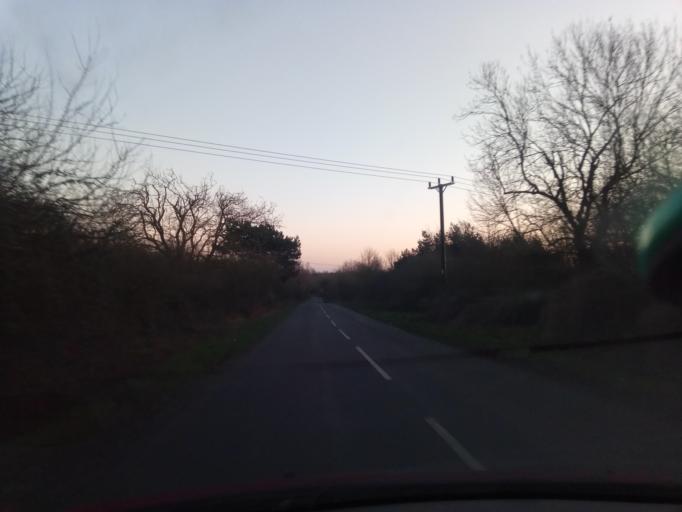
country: GB
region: England
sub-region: Leicestershire
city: Sileby
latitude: 52.7605
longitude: -1.1016
